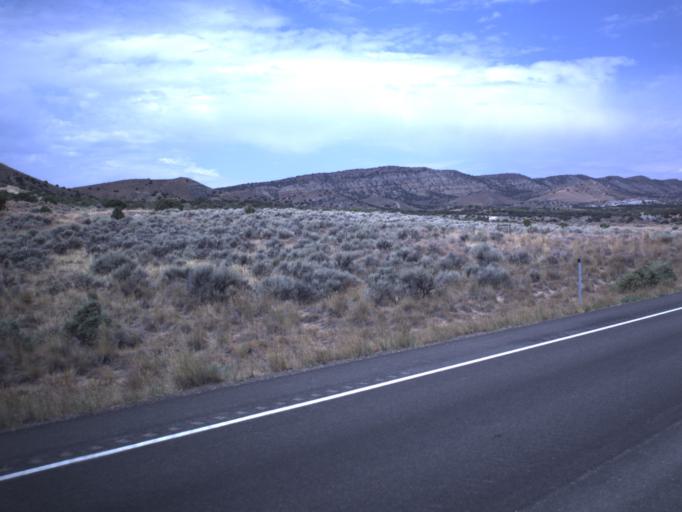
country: US
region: Utah
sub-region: Uintah County
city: Naples
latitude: 40.3537
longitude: -109.4948
